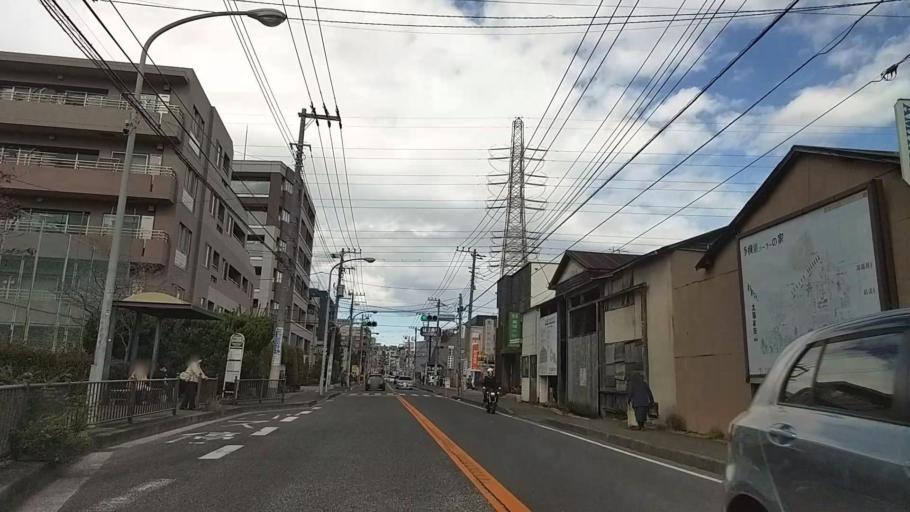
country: JP
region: Kanagawa
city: Yokohama
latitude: 35.5141
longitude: 139.6319
